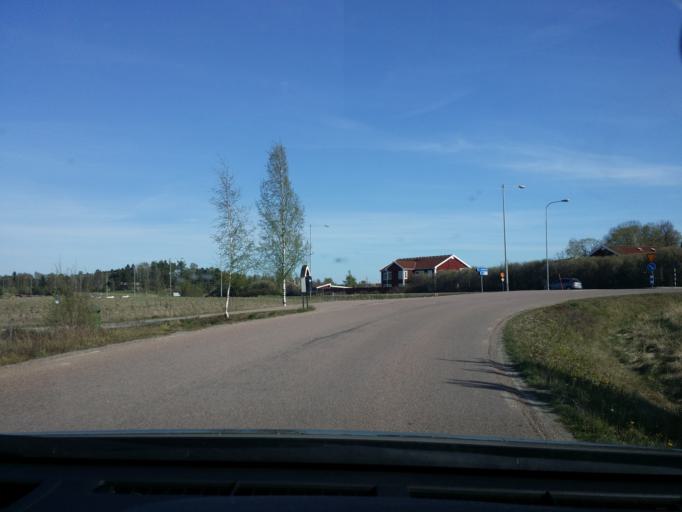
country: SE
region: Vaestmanland
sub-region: Vasteras
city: Vasteras
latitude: 59.6345
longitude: 16.4887
